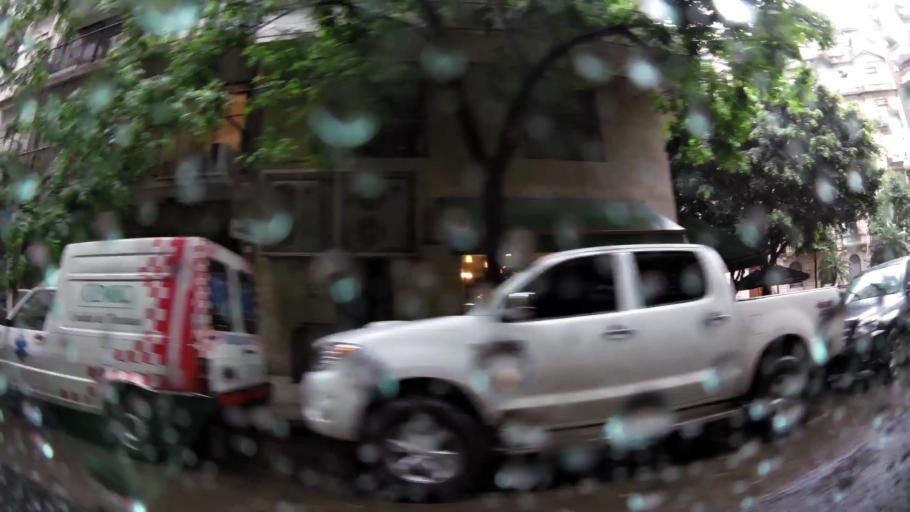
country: AR
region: Buenos Aires F.D.
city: Retiro
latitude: -34.5927
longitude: -58.3871
